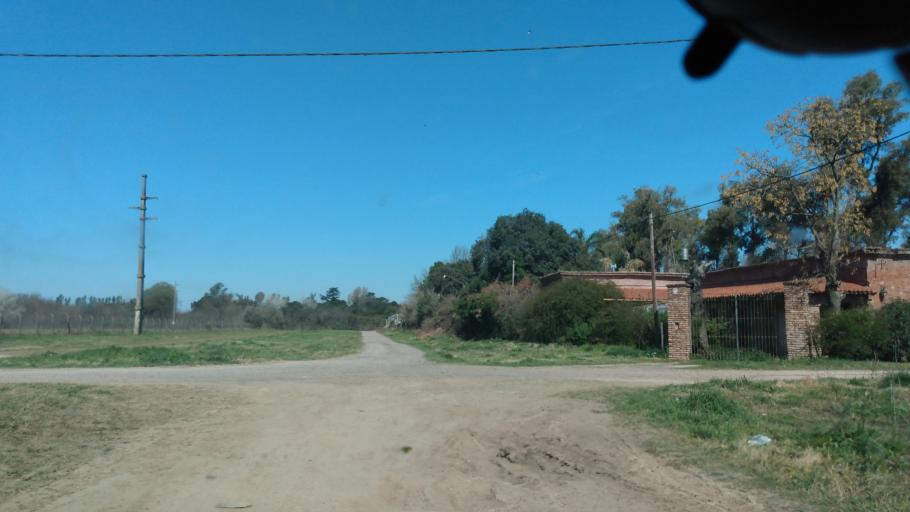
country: AR
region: Buenos Aires
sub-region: Partido de Lujan
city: Lujan
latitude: -34.5742
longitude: -59.1341
